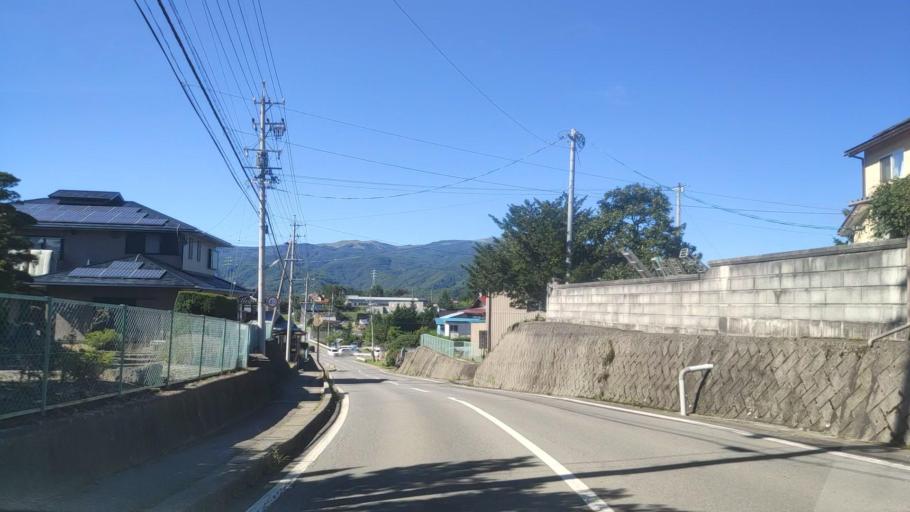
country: JP
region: Nagano
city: Chino
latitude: 36.0180
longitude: 138.2070
